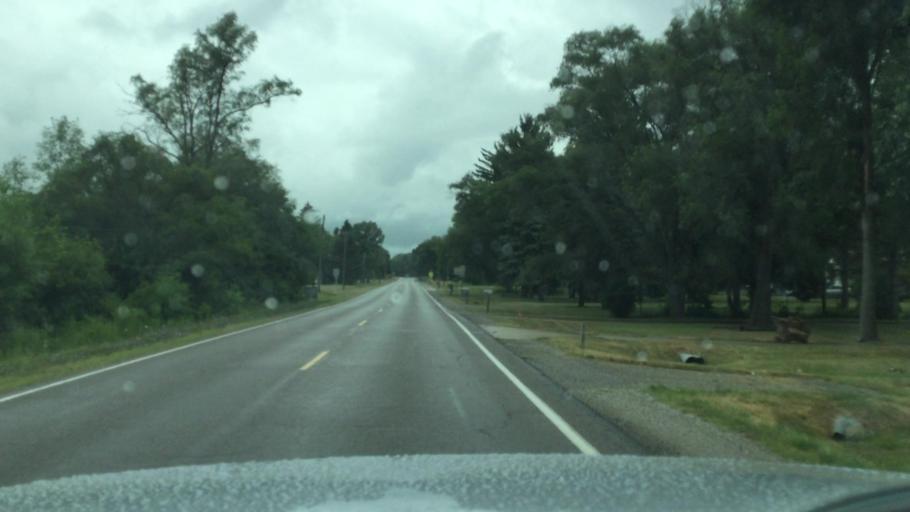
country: US
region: Michigan
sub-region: Genesee County
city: Beecher
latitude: 43.0752
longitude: -83.7370
